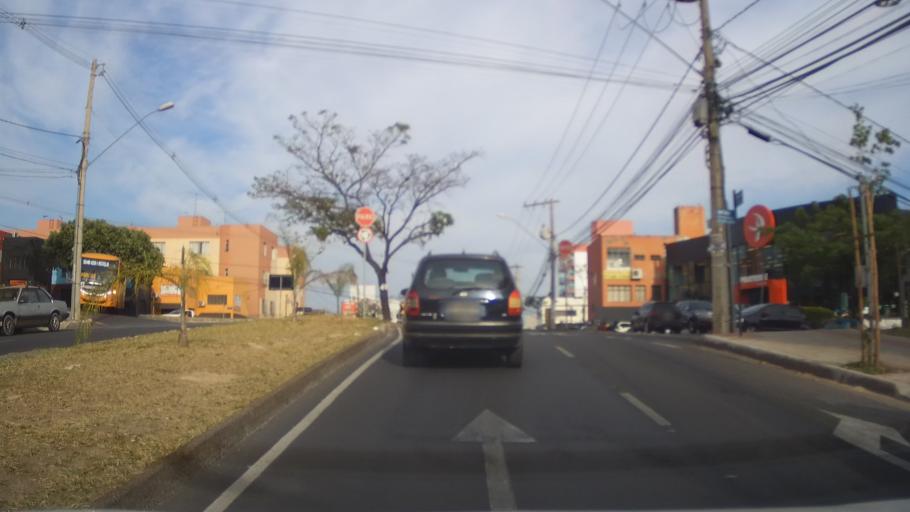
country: BR
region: Minas Gerais
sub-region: Belo Horizonte
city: Belo Horizonte
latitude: -19.8927
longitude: -43.9955
